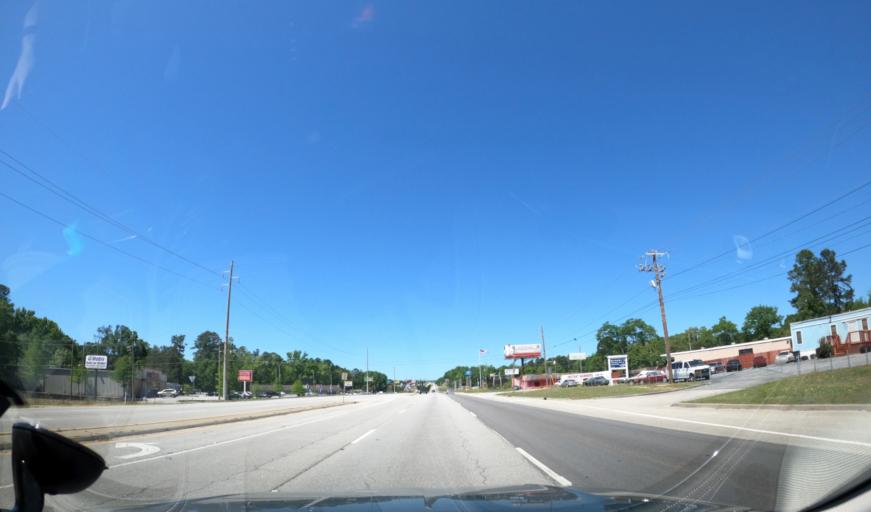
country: US
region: Georgia
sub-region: Columbia County
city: Martinez
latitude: 33.4525
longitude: -82.0541
